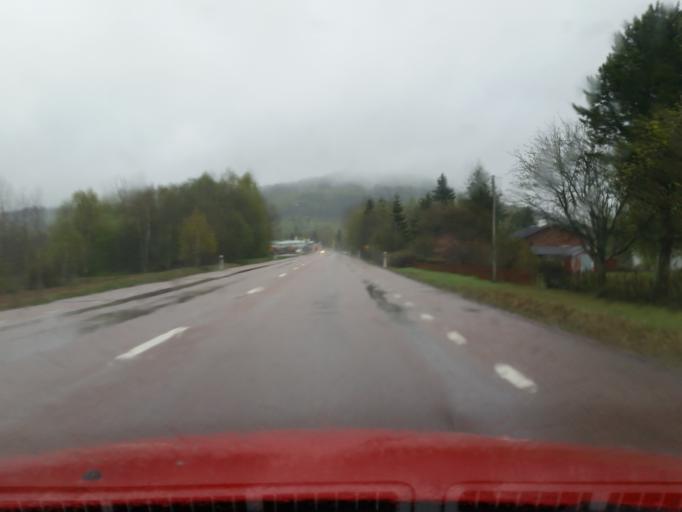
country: SE
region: Dalarna
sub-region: Gagnefs Kommun
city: Djuras
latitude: 60.5501
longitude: 15.2655
